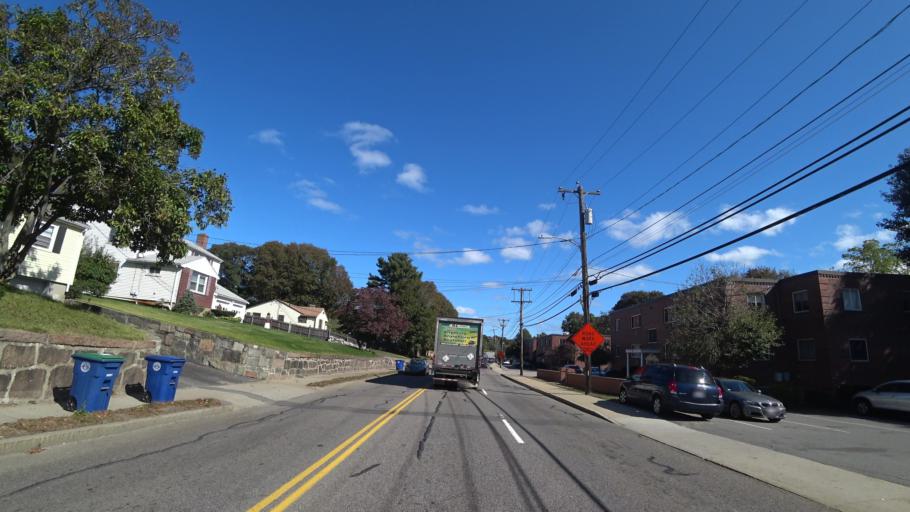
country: US
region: Massachusetts
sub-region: Norfolk County
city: Braintree
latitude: 42.2236
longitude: -70.9991
